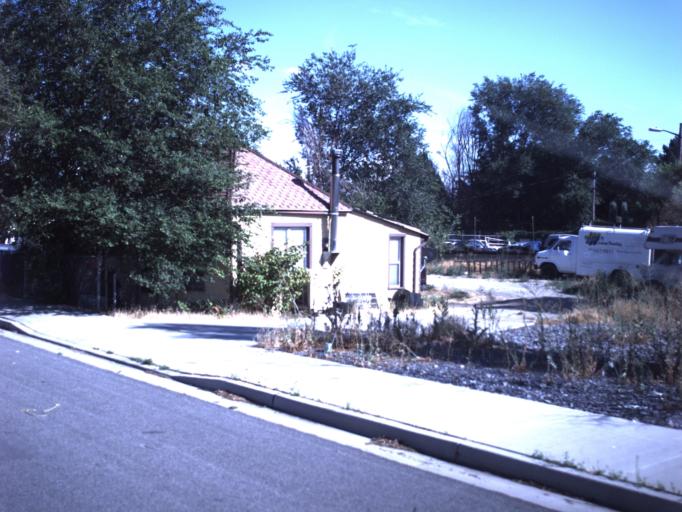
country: US
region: Utah
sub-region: Utah County
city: Lehi
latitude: 40.3950
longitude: -111.8427
